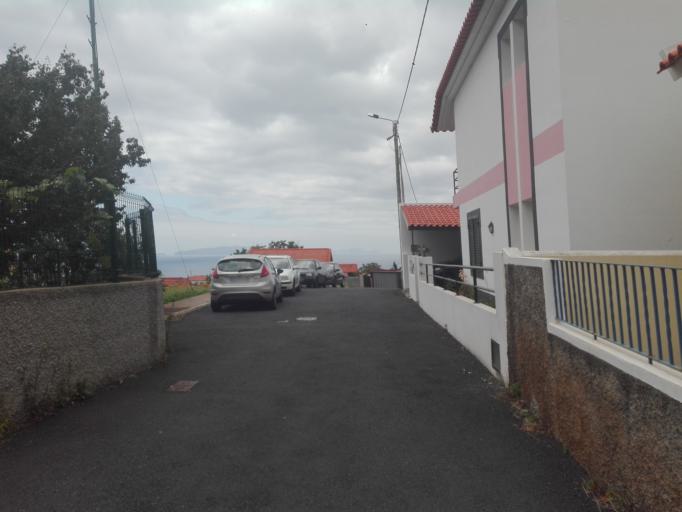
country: PT
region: Madeira
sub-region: Santa Cruz
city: Camacha
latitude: 32.6582
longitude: -16.8260
